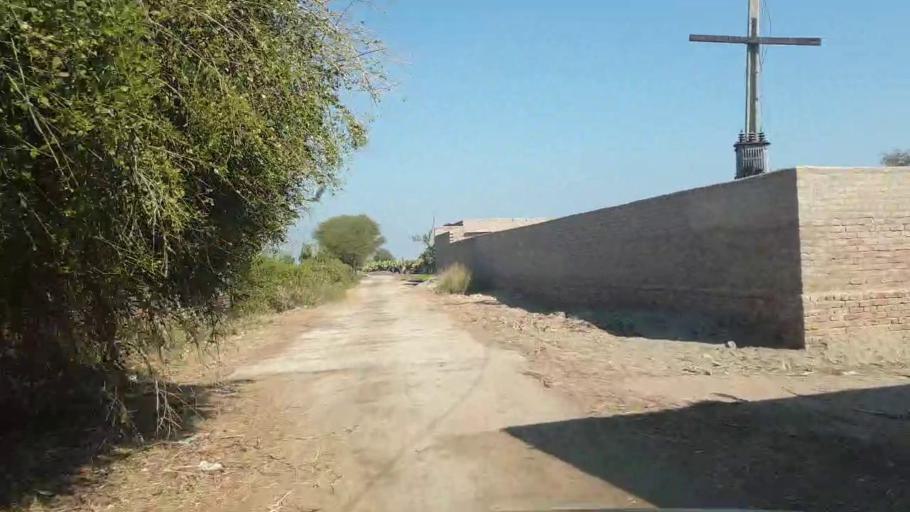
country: PK
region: Sindh
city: Shahdadpur
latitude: 25.9157
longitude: 68.5853
